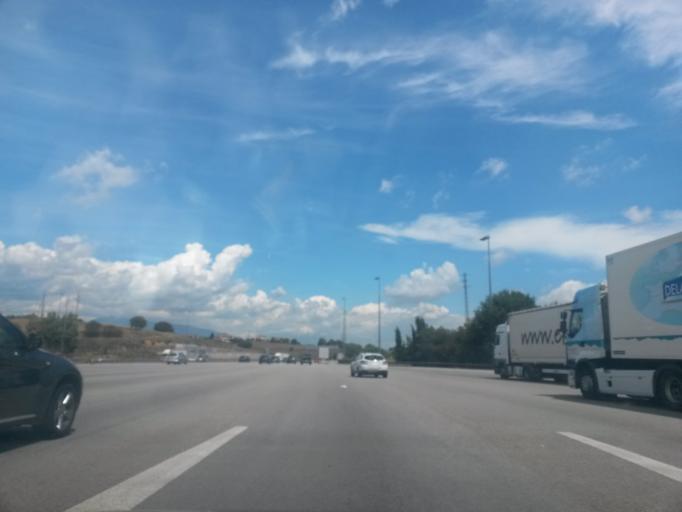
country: ES
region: Catalonia
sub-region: Provincia de Barcelona
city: La Roca del Valles
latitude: 41.5928
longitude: 2.3116
